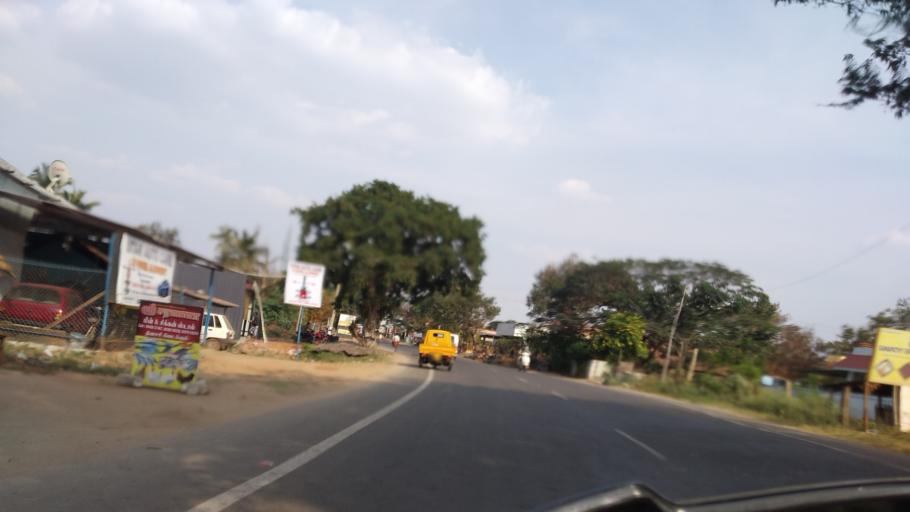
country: IN
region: Tamil Nadu
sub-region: Coimbatore
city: Perur
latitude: 10.9711
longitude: 76.8849
